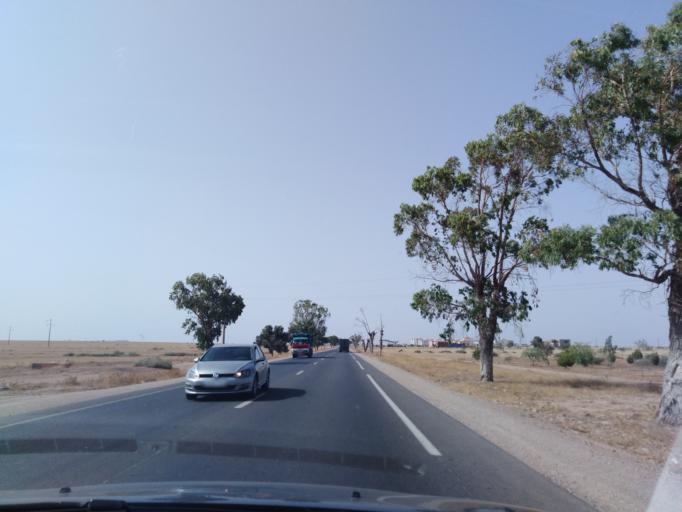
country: MA
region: Marrakech-Tensift-Al Haouz
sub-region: Kelaa-Des-Sraghna
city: Sidi Bou Othmane
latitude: 32.2125
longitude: -7.9567
